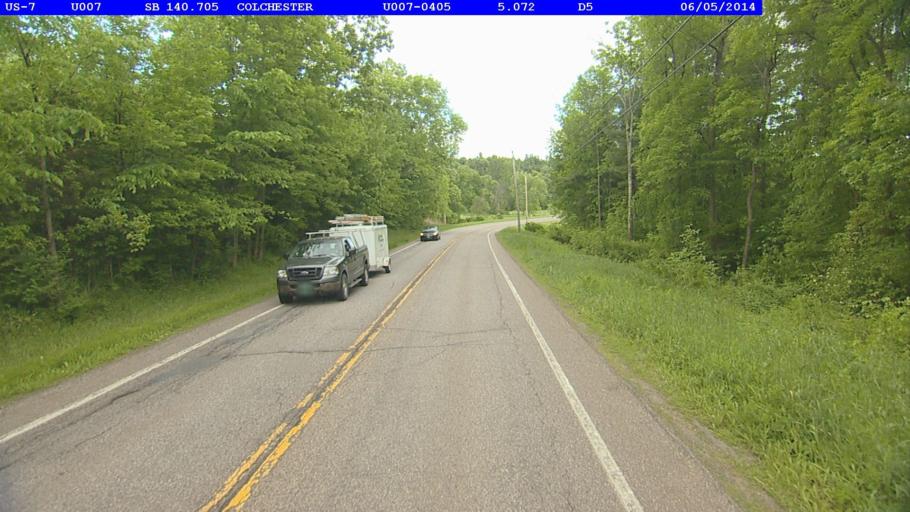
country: US
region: Vermont
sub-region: Chittenden County
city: Colchester
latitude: 44.5706
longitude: -73.1557
